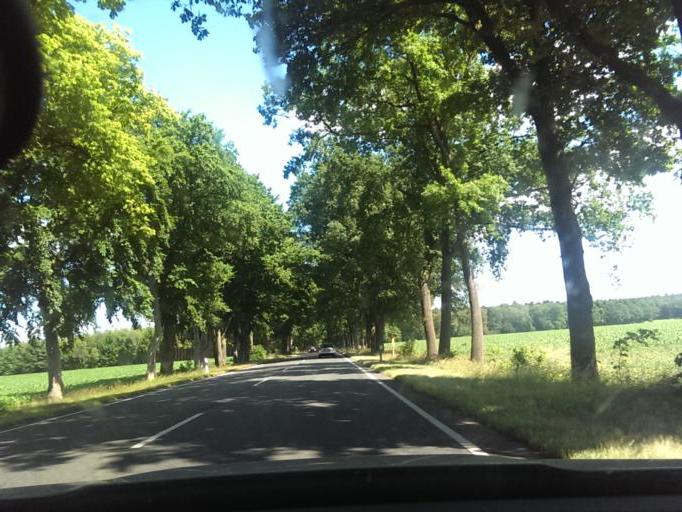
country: DE
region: Lower Saxony
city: Kirchlinteln
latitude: 52.9857
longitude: 9.2631
